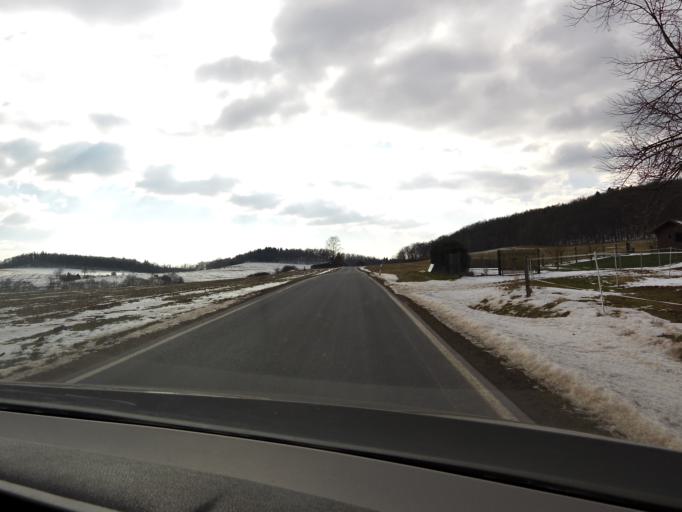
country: DE
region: Thuringia
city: Wolfsburg-Unkeroda
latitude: 50.8925
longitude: 10.2930
